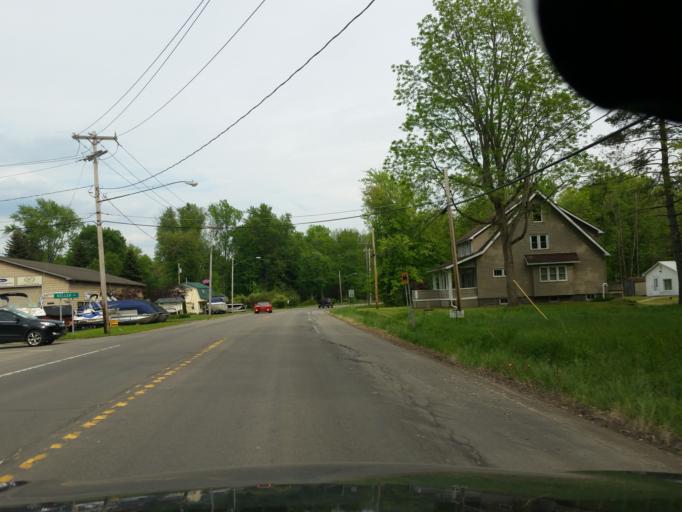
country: US
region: New York
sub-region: Chautauqua County
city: Lakewood
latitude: 42.1039
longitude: -79.3612
